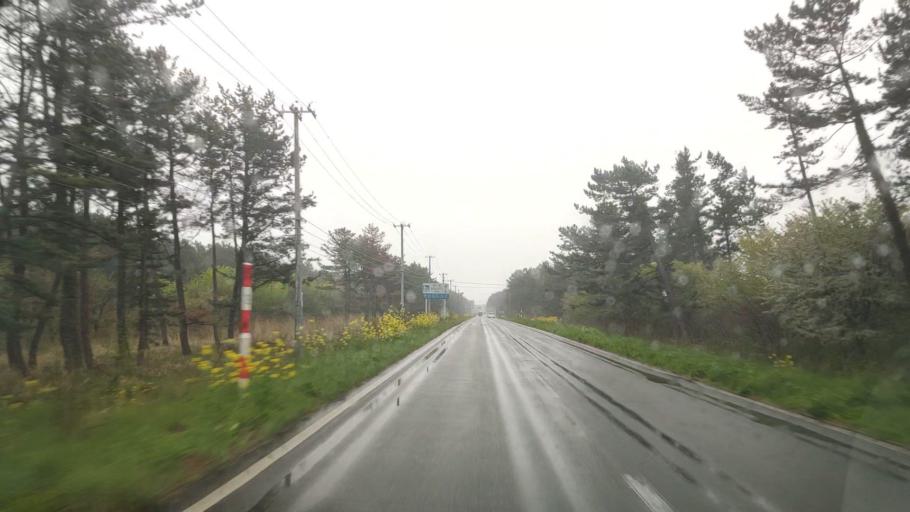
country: JP
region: Akita
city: Tenno
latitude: 40.0249
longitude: 139.9527
